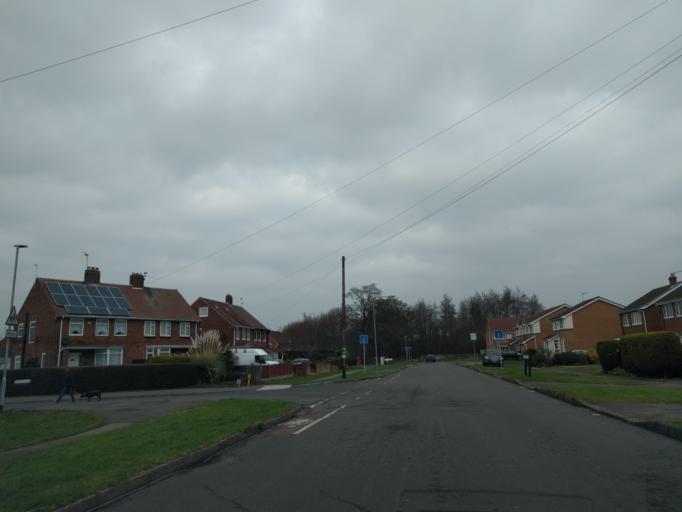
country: GB
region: England
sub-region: Nottinghamshire
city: Newark on Trent
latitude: 53.0934
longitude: -0.7939
